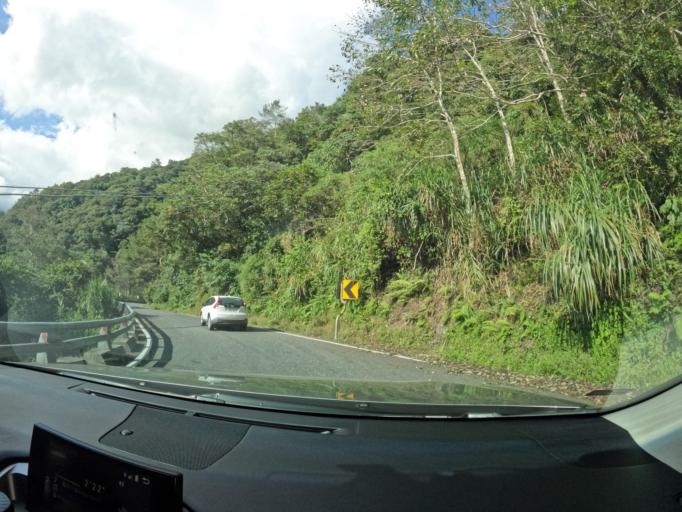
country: TW
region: Taiwan
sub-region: Taitung
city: Taitung
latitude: 23.1987
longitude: 121.0217
